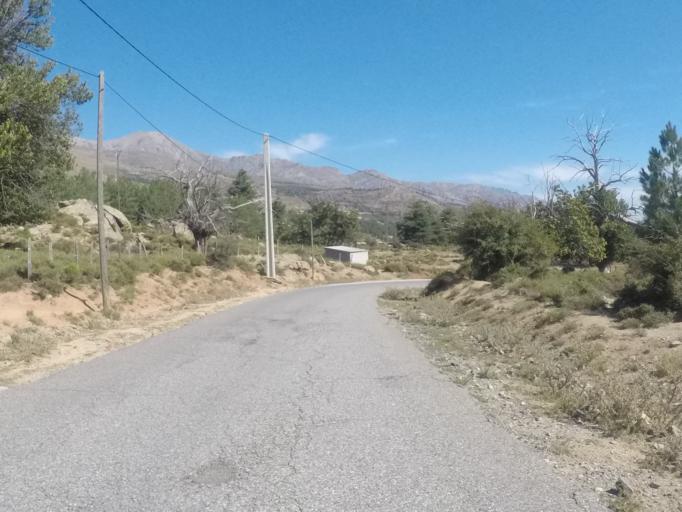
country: FR
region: Corsica
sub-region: Departement de la Haute-Corse
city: Corte
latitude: 42.3145
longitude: 8.9700
